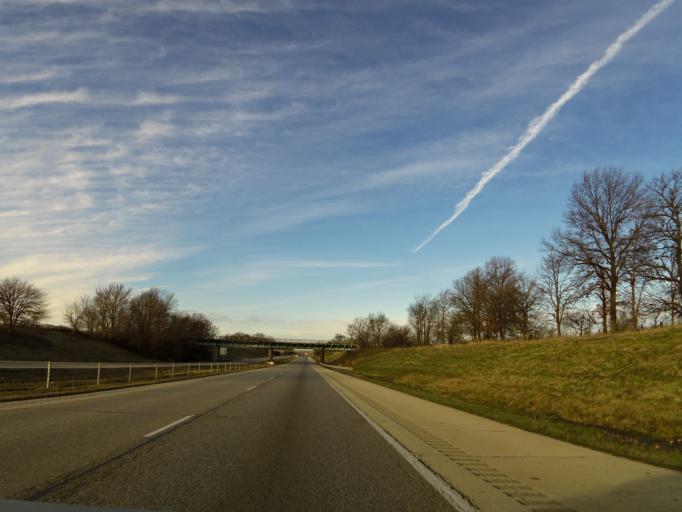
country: US
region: Illinois
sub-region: Vermilion County
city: Danville
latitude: 40.1156
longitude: -87.5573
